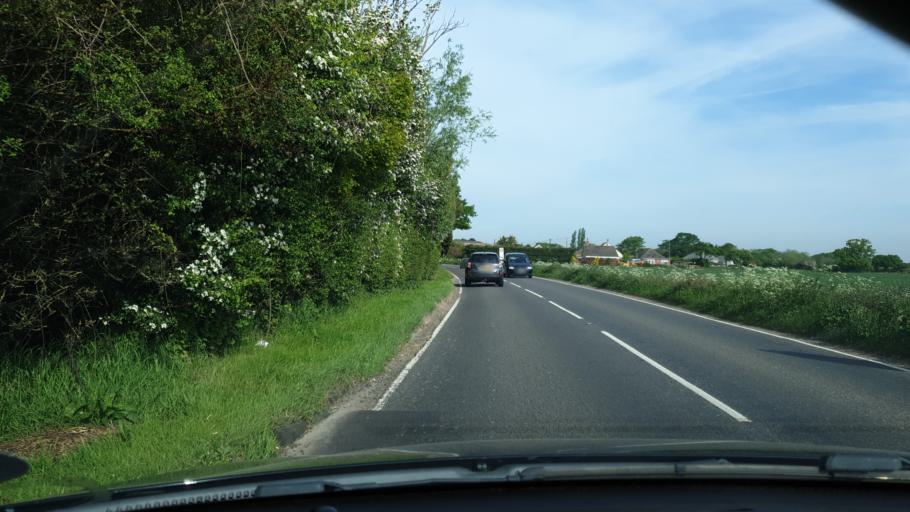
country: GB
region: England
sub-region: Essex
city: Little Clacton
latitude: 51.8525
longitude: 1.1849
